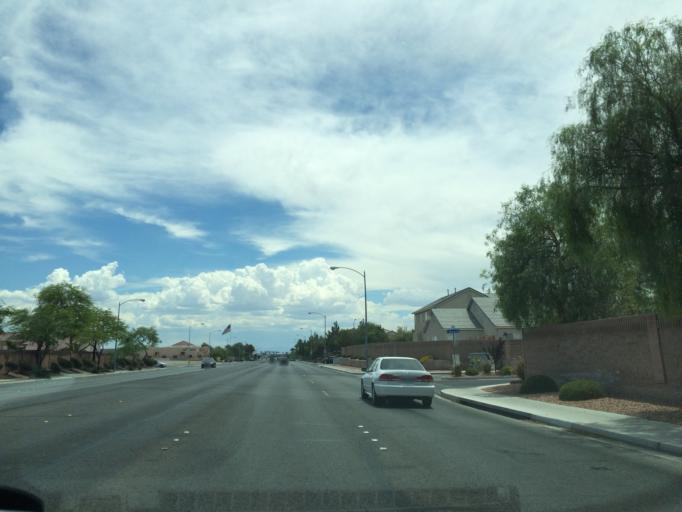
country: US
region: Nevada
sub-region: Clark County
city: North Las Vegas
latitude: 36.2667
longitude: -115.1801
